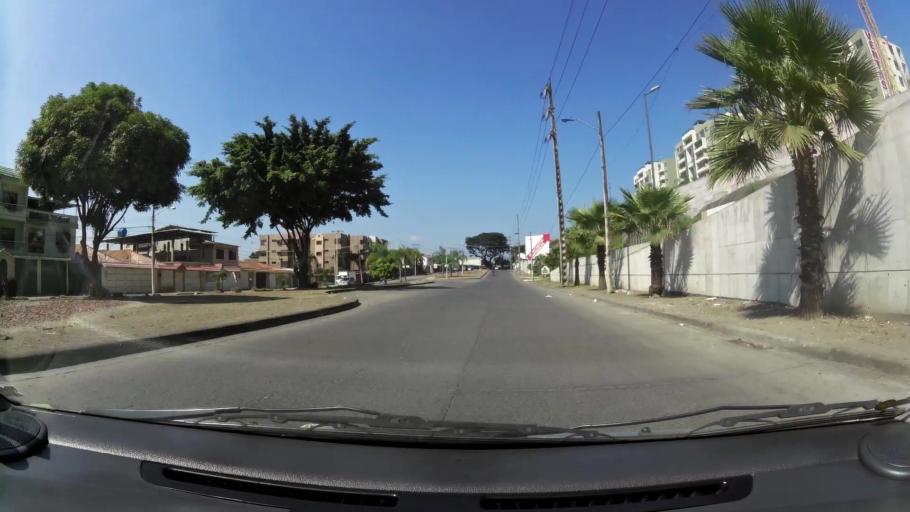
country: EC
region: Guayas
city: Guayaquil
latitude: -2.1341
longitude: -79.9141
